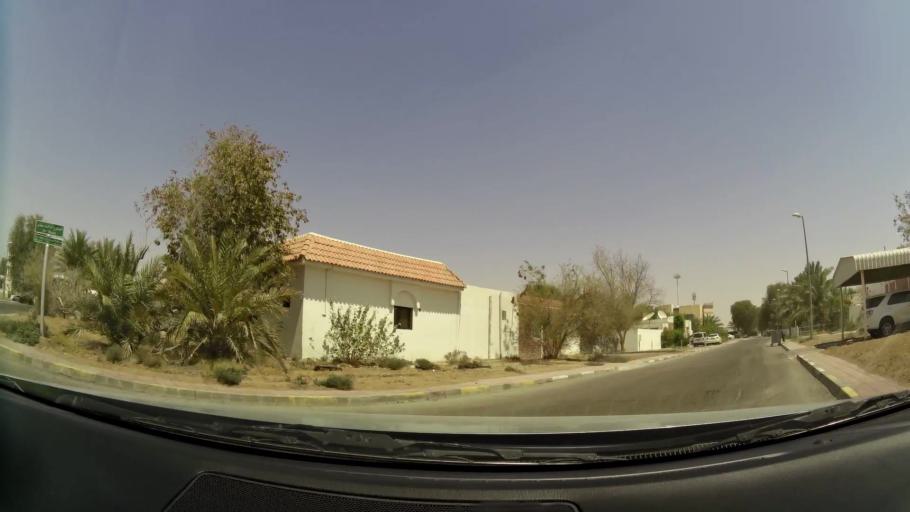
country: OM
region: Al Buraimi
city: Al Buraymi
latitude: 24.2743
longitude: 55.7681
